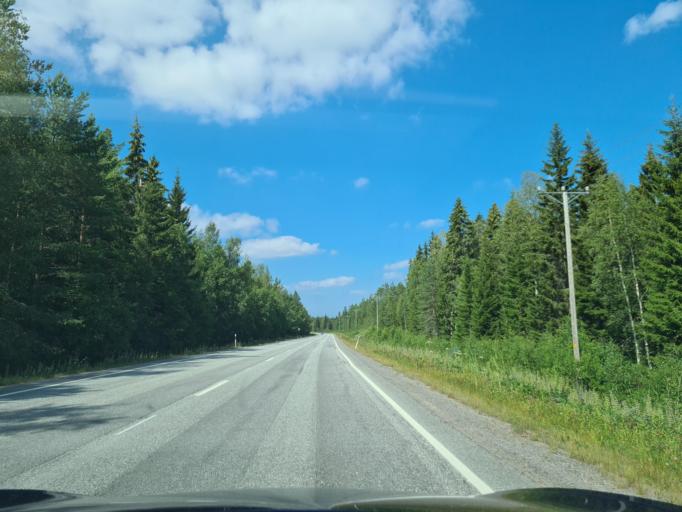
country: FI
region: Ostrobothnia
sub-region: Vaasa
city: Vaasa
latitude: 63.1748
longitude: 21.5782
